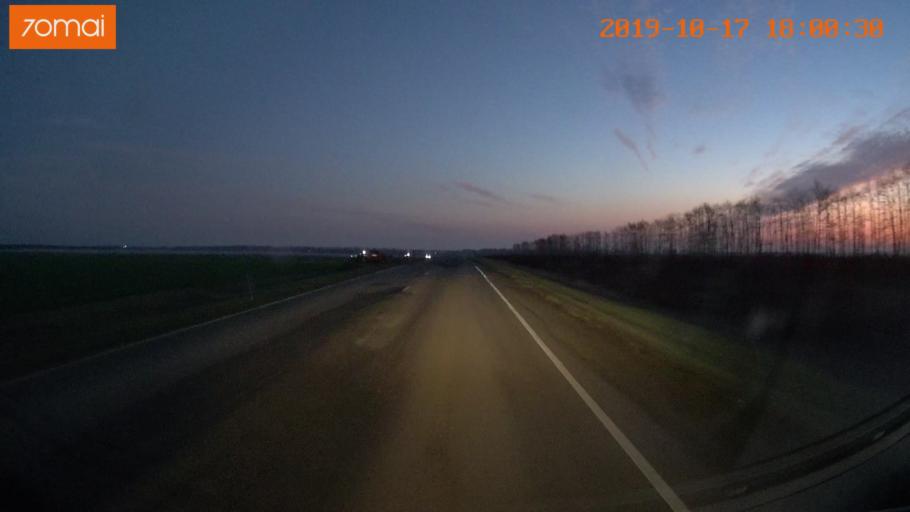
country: RU
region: Tula
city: Kurkino
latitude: 53.5204
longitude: 38.6149
